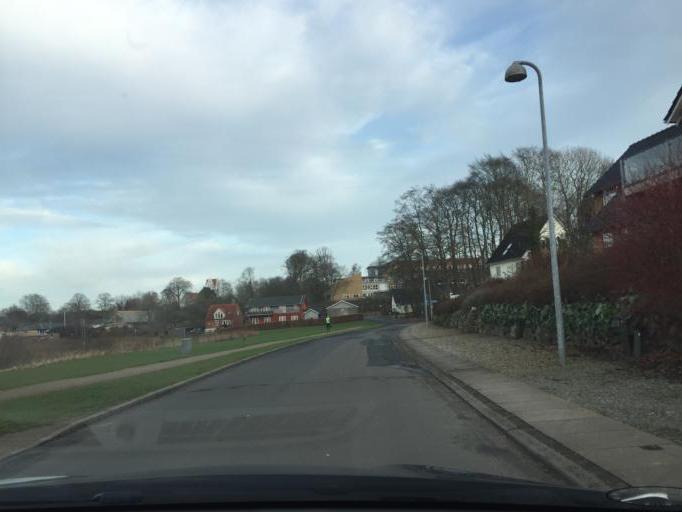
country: DK
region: South Denmark
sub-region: Faaborg-Midtfyn Kommune
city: Ringe
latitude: 55.2361
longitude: 10.4727
